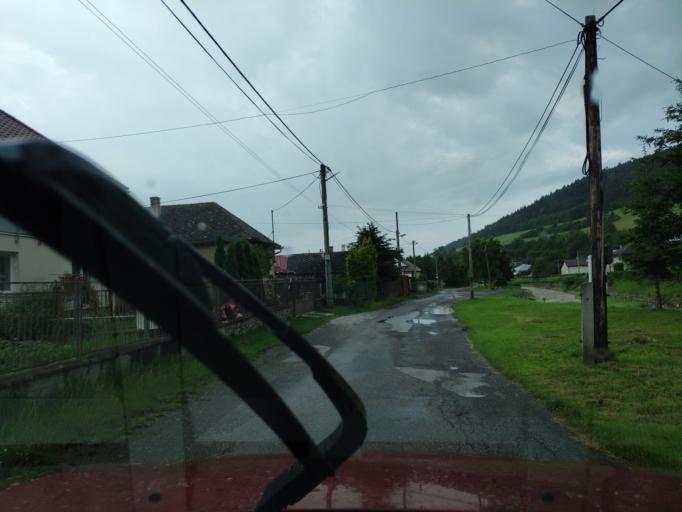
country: SK
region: Presovsky
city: Sabinov
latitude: 49.0221
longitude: 21.0231
